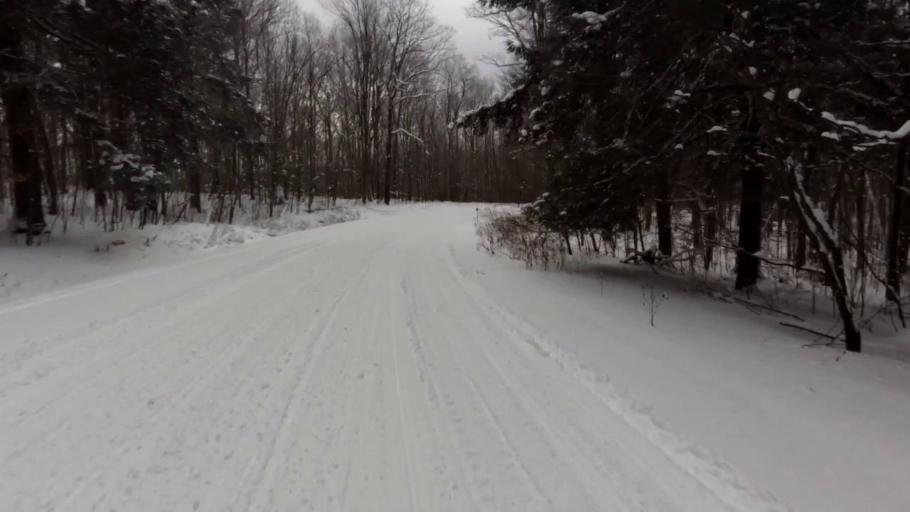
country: US
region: New York
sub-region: Cattaraugus County
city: Salamanca
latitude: 42.0558
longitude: -78.7603
